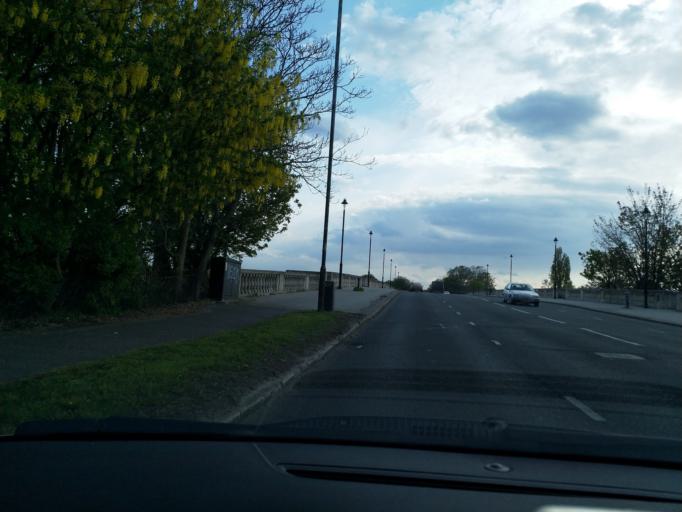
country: GB
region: England
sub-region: Greater London
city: Richmond
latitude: 51.4739
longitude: -0.2685
